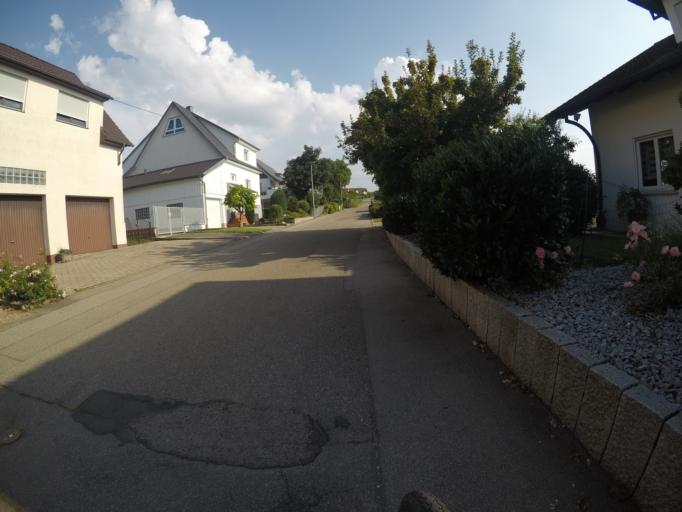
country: DE
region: Baden-Wuerttemberg
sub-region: Tuebingen Region
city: Pliezhausen
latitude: 48.5605
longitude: 9.2313
